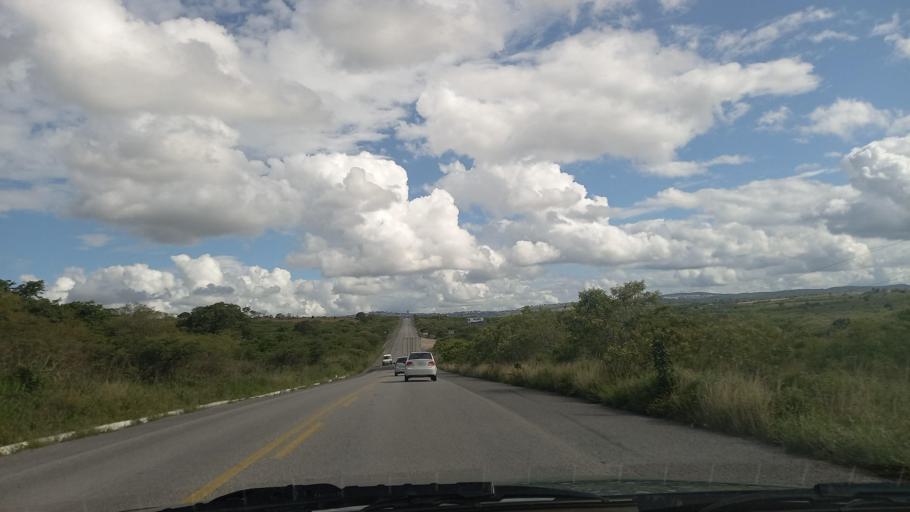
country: BR
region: Pernambuco
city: Garanhuns
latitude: -8.8121
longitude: -36.4445
